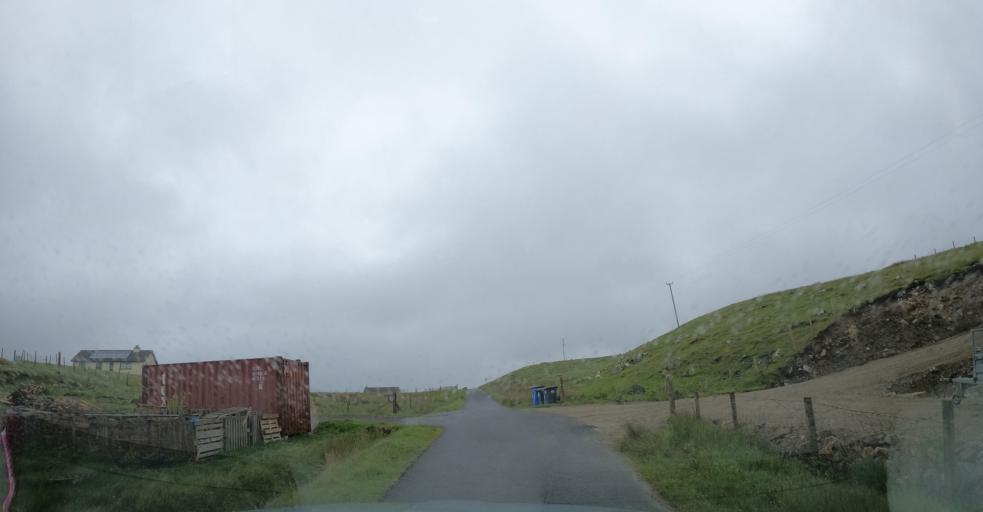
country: GB
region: Scotland
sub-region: Eilean Siar
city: Isle of North Uist
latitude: 57.5515
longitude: -7.2071
